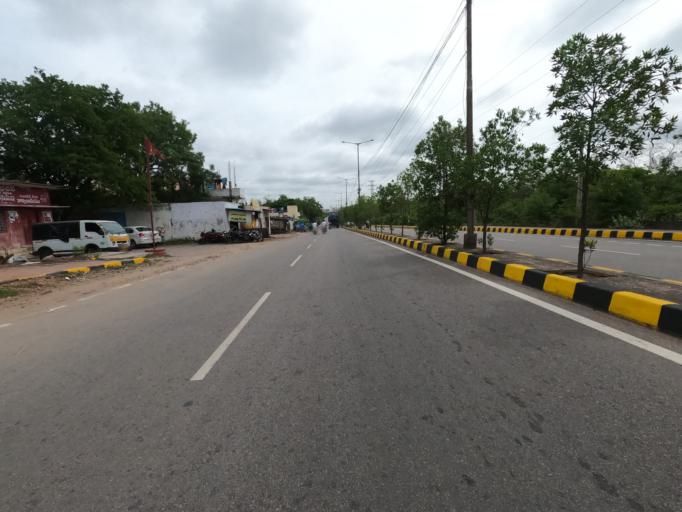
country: IN
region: Telangana
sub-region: Hyderabad
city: Hyderabad
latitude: 17.3373
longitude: 78.4120
